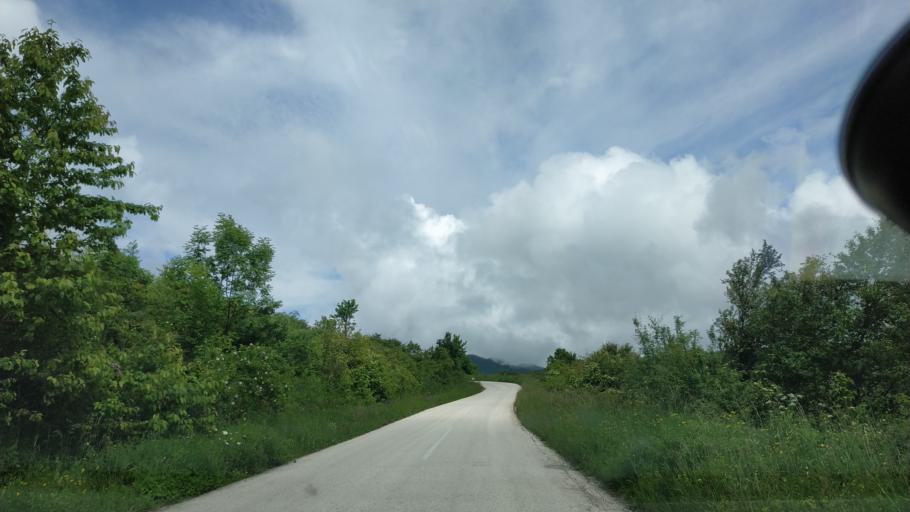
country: RS
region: Central Serbia
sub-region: Zajecarski Okrug
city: Boljevac
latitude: 43.7466
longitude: 21.9471
